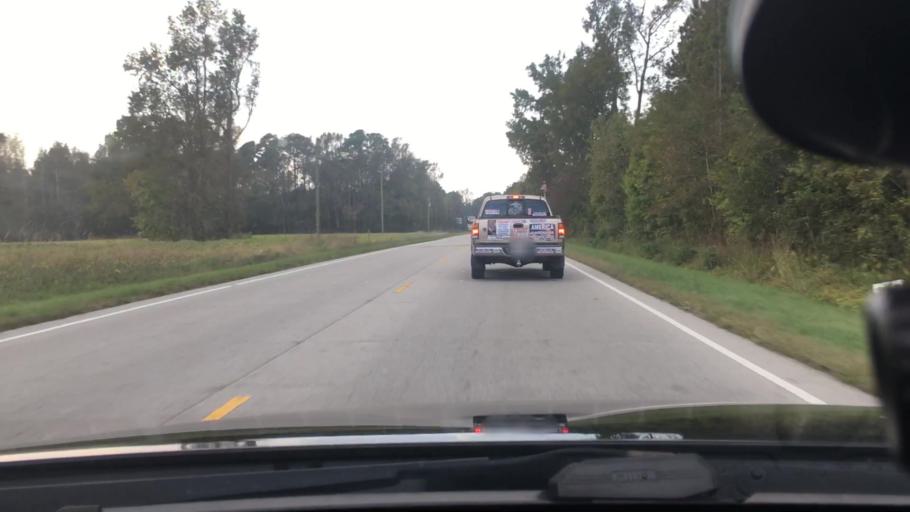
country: US
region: North Carolina
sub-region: Craven County
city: Vanceboro
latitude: 35.2758
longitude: -77.1175
